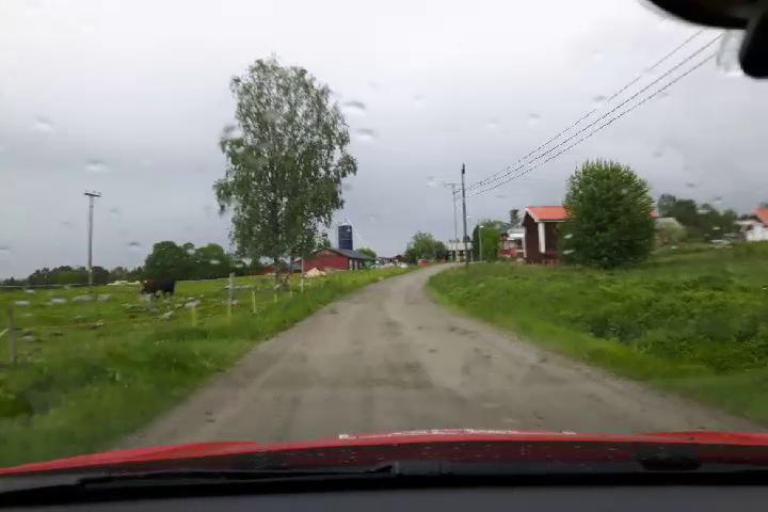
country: SE
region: Jaemtland
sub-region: Bergs Kommun
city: Hoverberg
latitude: 62.7369
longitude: 14.4552
